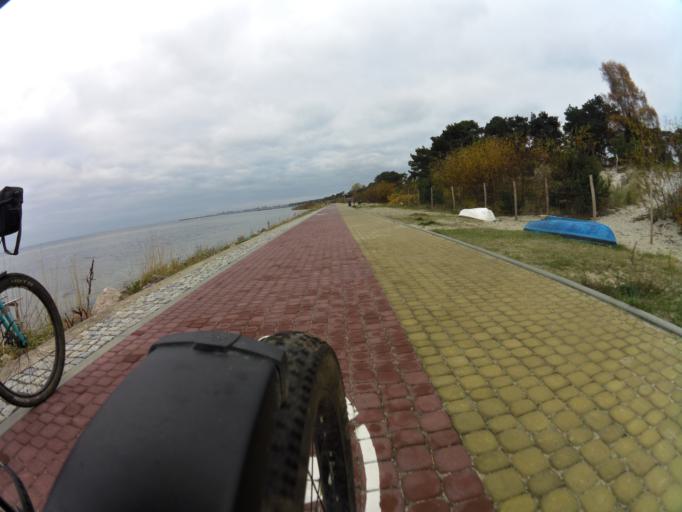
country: PL
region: Pomeranian Voivodeship
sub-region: Powiat pucki
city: Jastarnia
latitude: 54.6770
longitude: 18.7173
